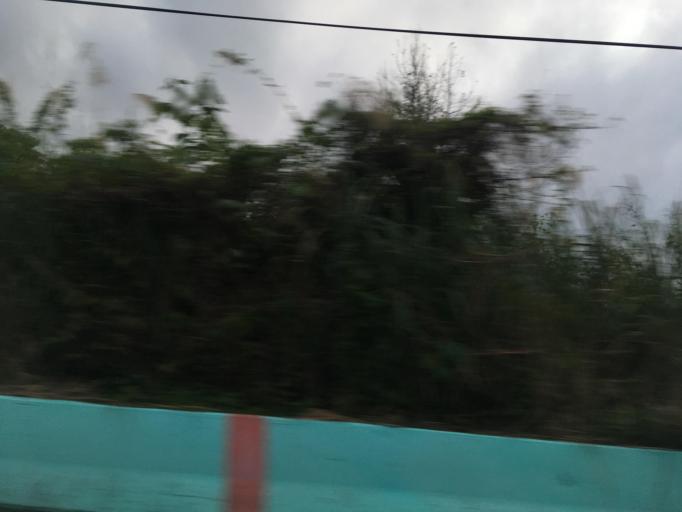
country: TW
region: Taiwan
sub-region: Yilan
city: Yilan
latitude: 24.7477
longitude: 121.7187
